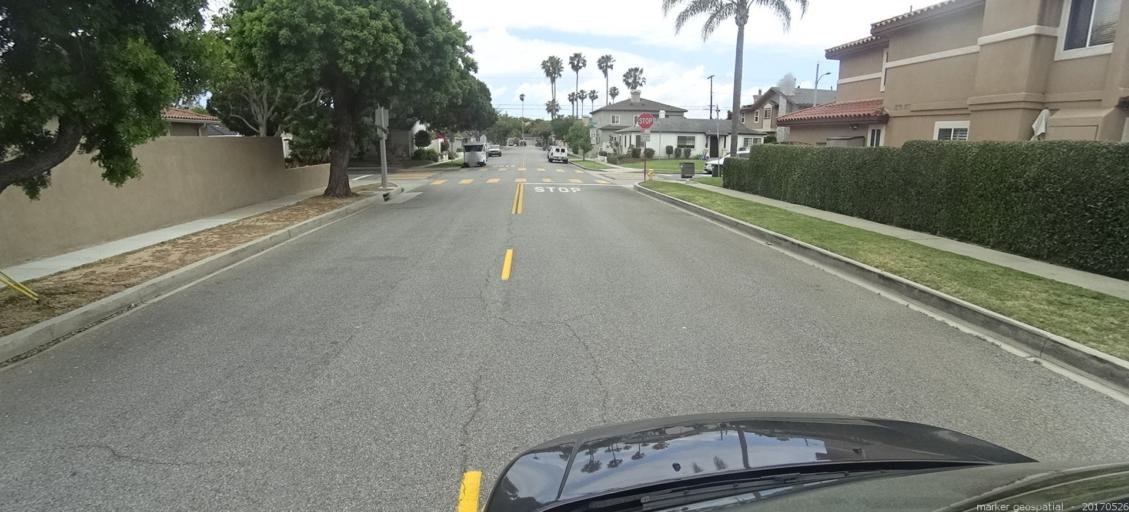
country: US
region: California
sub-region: Los Angeles County
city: Lawndale
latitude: 33.8637
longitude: -118.3631
